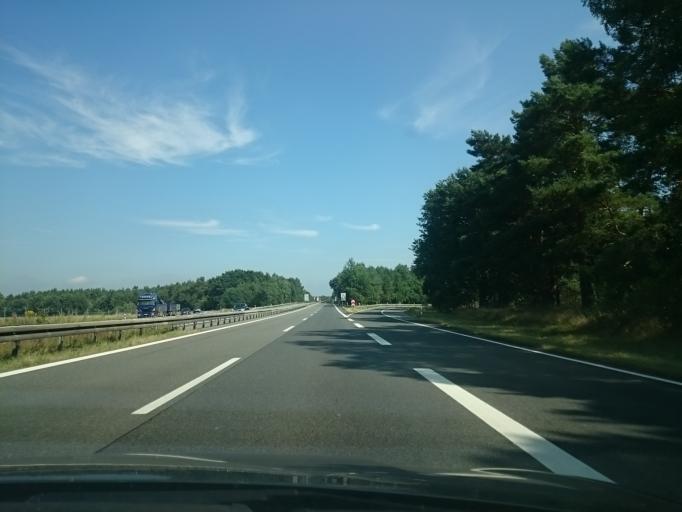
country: DE
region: Brandenburg
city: Lubbenau
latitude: 51.8405
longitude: 13.9210
